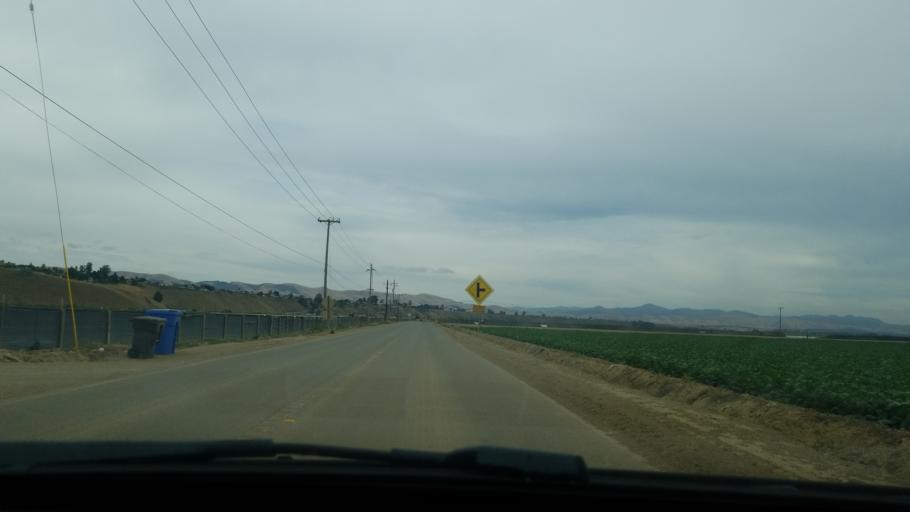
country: US
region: California
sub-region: Santa Barbara County
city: Guadalupe
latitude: 35.0032
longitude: -120.5212
